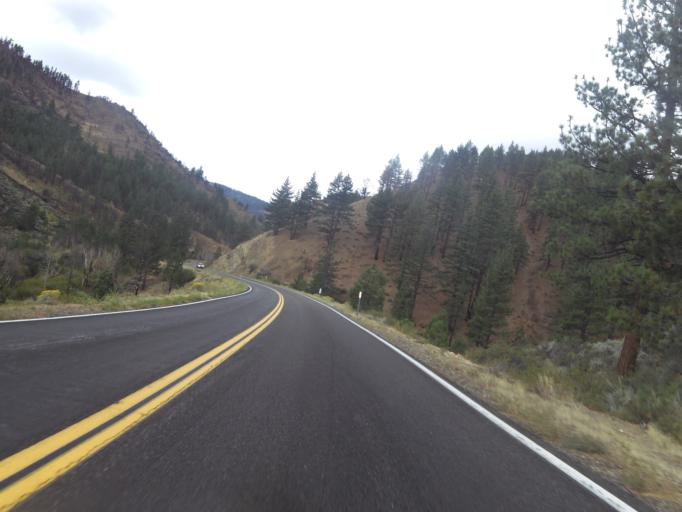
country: US
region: Nevada
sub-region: Douglas County
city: Gardnerville Ranchos
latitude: 38.6658
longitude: -119.6932
